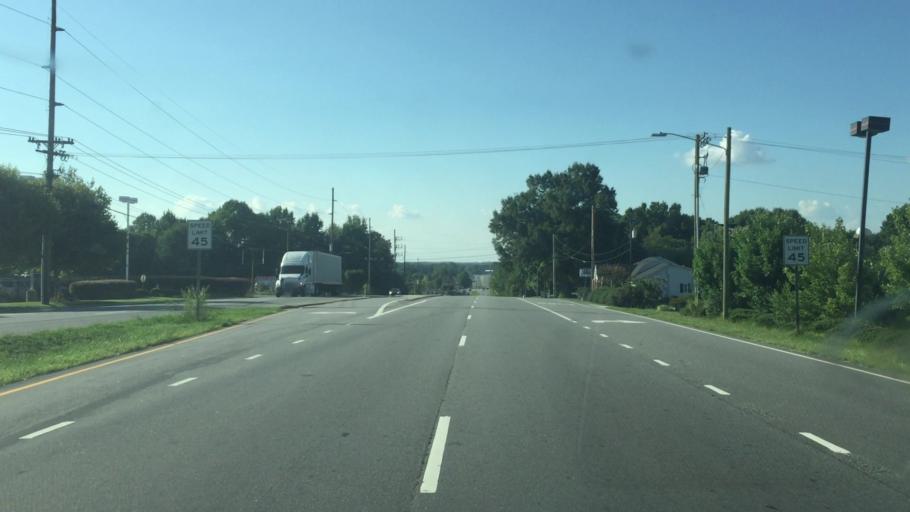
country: US
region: North Carolina
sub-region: Cabarrus County
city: Concord
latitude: 35.4027
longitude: -80.6091
